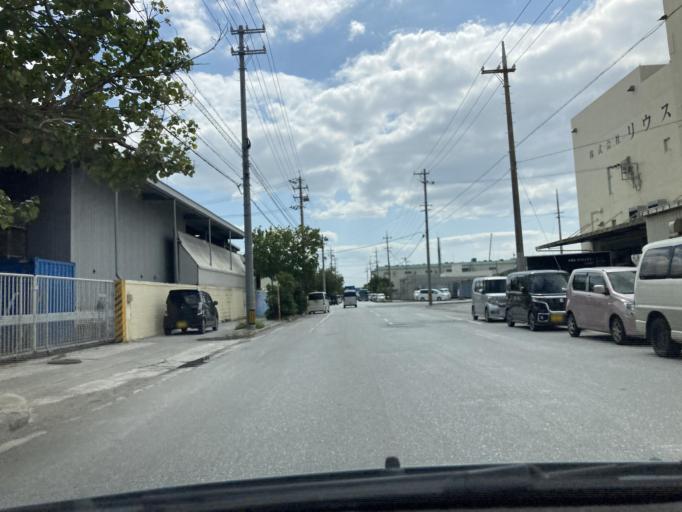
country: JP
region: Okinawa
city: Naha-shi
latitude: 26.2442
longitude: 127.6733
